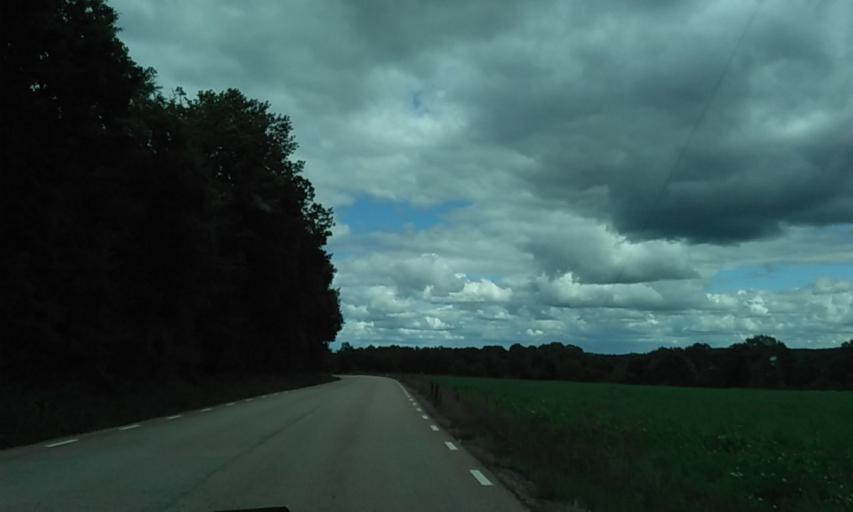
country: SE
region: Vaestra Goetaland
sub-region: Boras Kommun
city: Boras
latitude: 57.7997
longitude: 12.8882
